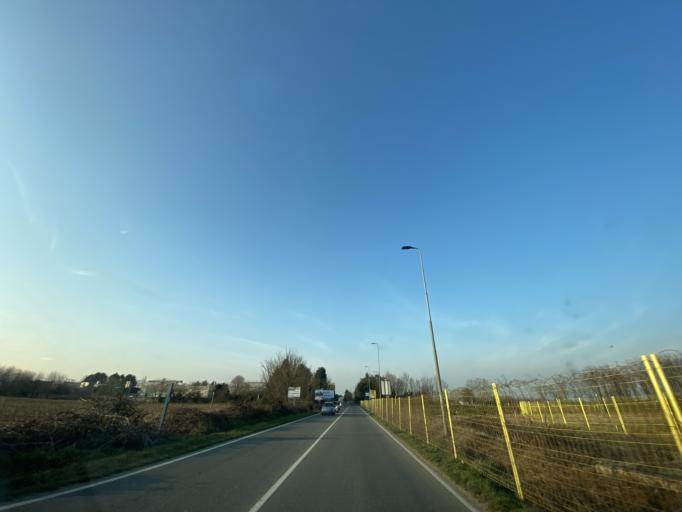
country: IT
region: Lombardy
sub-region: Citta metropolitana di Milano
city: Passirana
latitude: 45.5442
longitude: 9.0328
